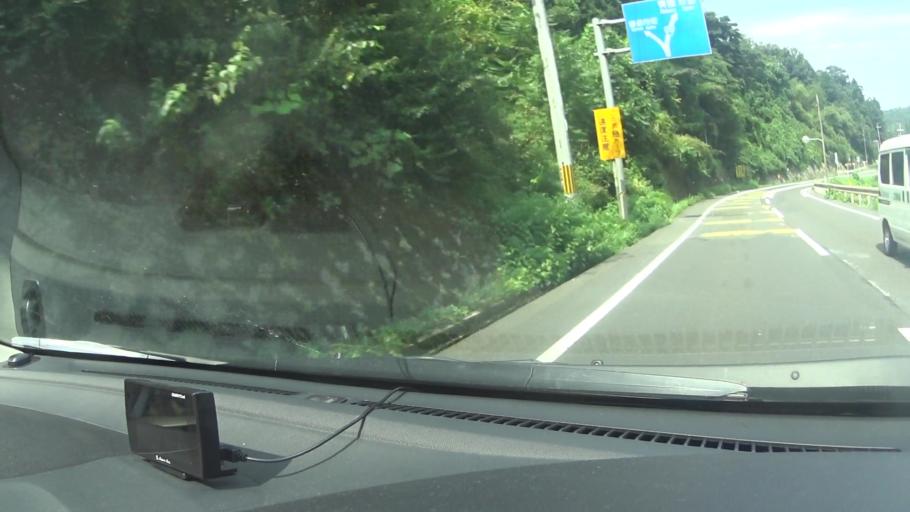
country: JP
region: Kyoto
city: Ayabe
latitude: 35.2876
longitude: 135.2660
